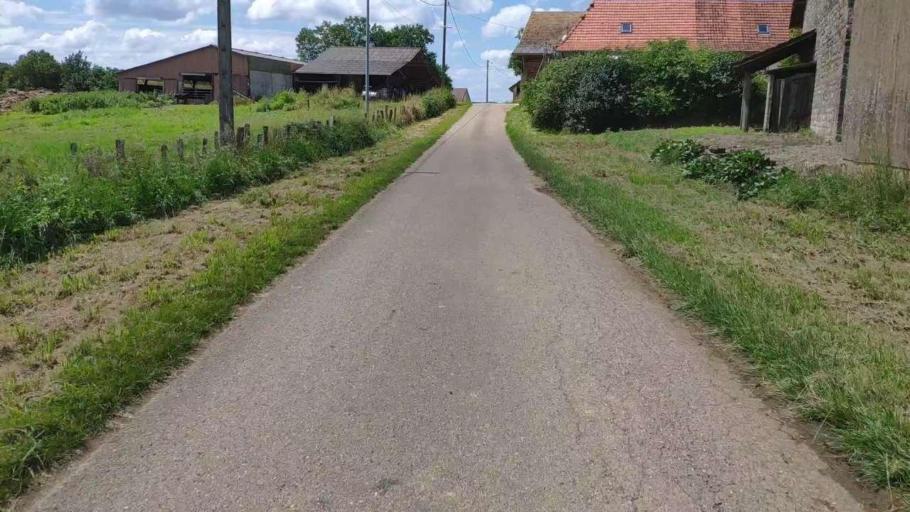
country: FR
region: Franche-Comte
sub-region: Departement du Jura
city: Bletterans
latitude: 46.8486
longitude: 5.4425
